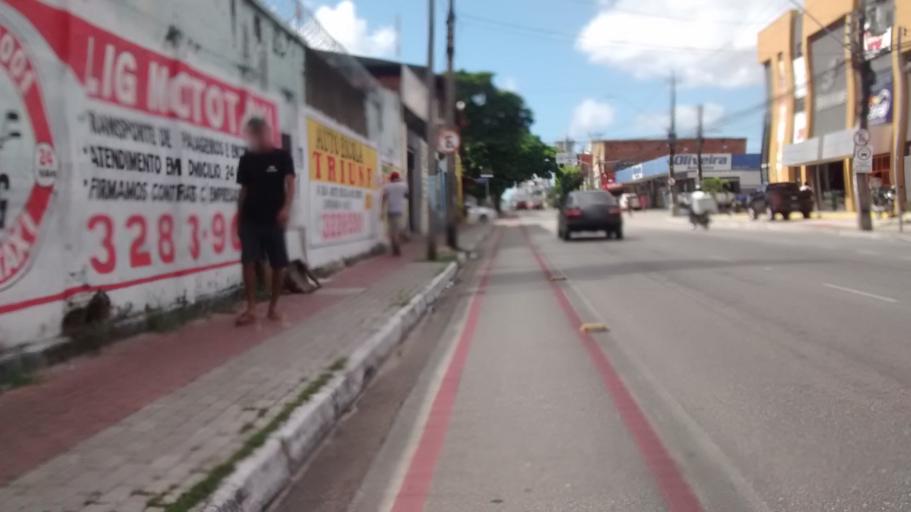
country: BR
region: Ceara
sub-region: Fortaleza
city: Fortaleza
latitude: -3.7400
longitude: -38.5197
